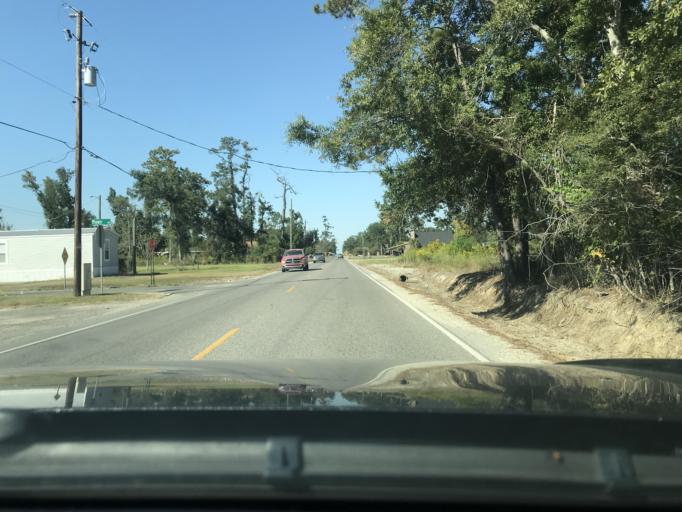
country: US
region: Louisiana
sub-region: Calcasieu Parish
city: Moss Bluff
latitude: 30.3077
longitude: -93.2001
